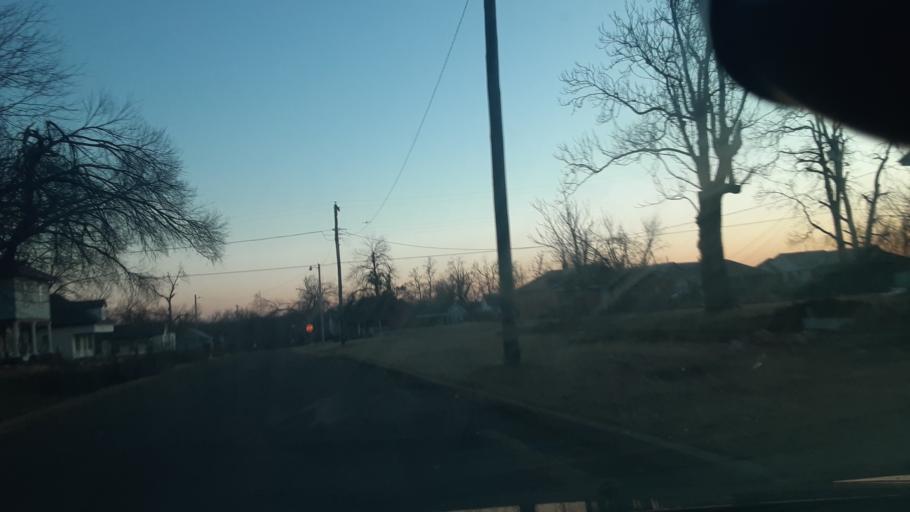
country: US
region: Oklahoma
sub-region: Logan County
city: Guthrie
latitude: 35.8748
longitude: -97.4202
